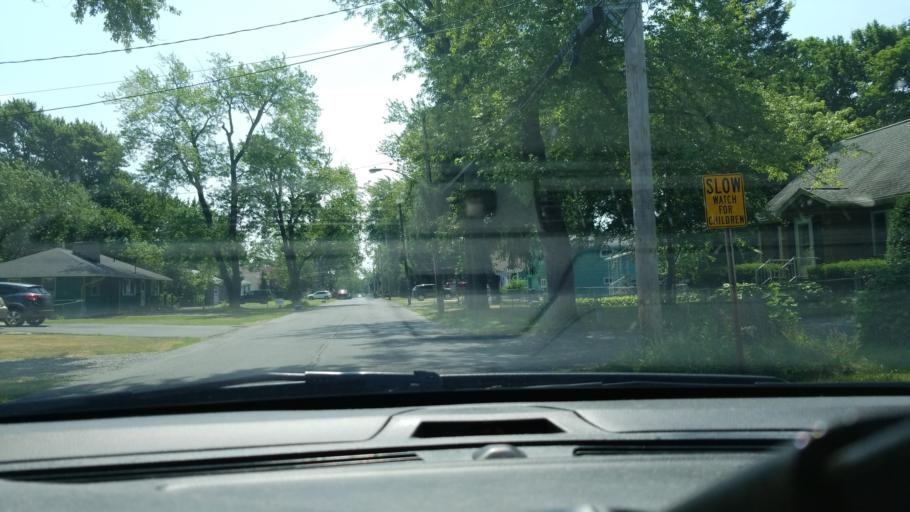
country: US
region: New York
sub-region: Onondaga County
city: Galeville
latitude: 43.0906
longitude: -76.1789
